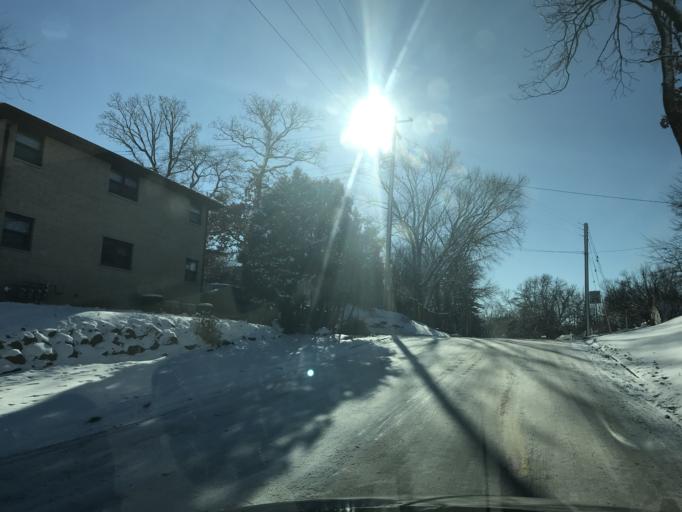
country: US
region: Wisconsin
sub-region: Dane County
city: Monona
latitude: 43.0837
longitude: -89.3205
